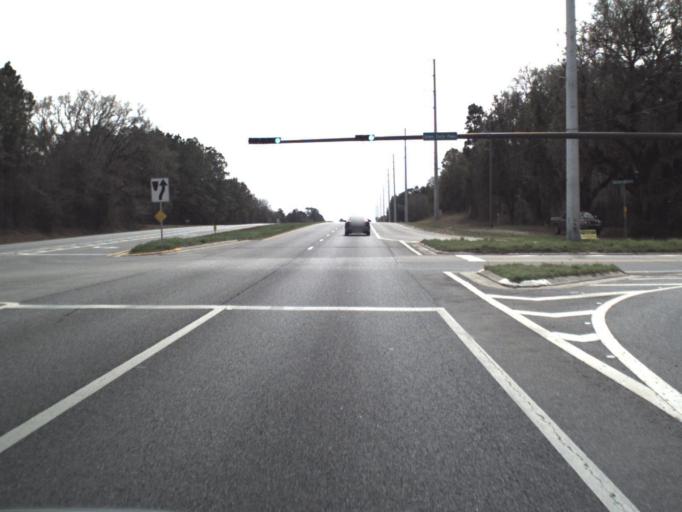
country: US
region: Florida
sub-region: Washington County
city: Chipley
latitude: 30.7341
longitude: -85.3865
